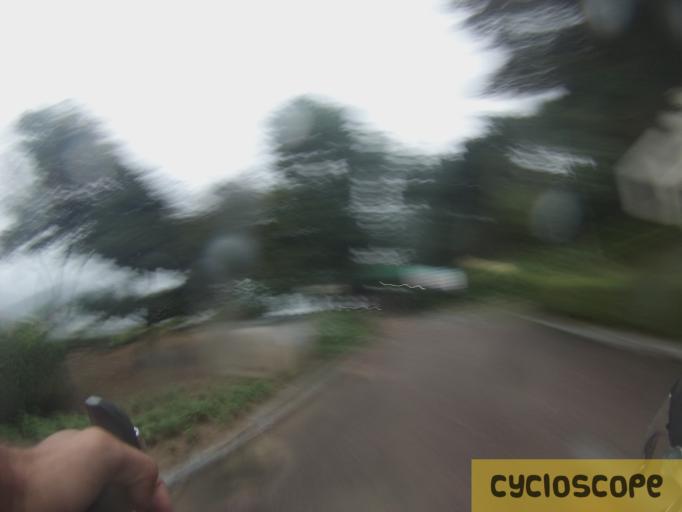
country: KR
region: Chungcheongnam-do
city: Yesan
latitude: 36.7283
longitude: 126.8553
